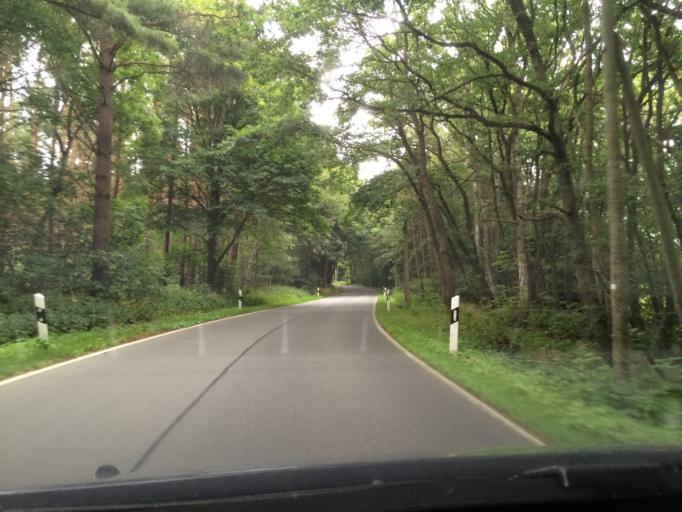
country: DE
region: Mecklenburg-Vorpommern
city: Prohn
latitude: 54.4232
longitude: 13.0221
